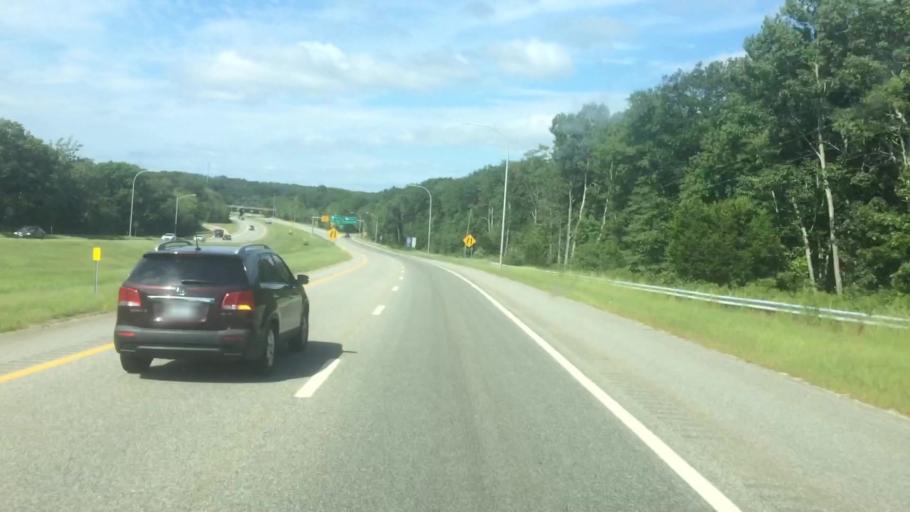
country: US
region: Rhode Island
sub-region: Washington County
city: North Kingstown
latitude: 41.5315
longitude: -71.4579
